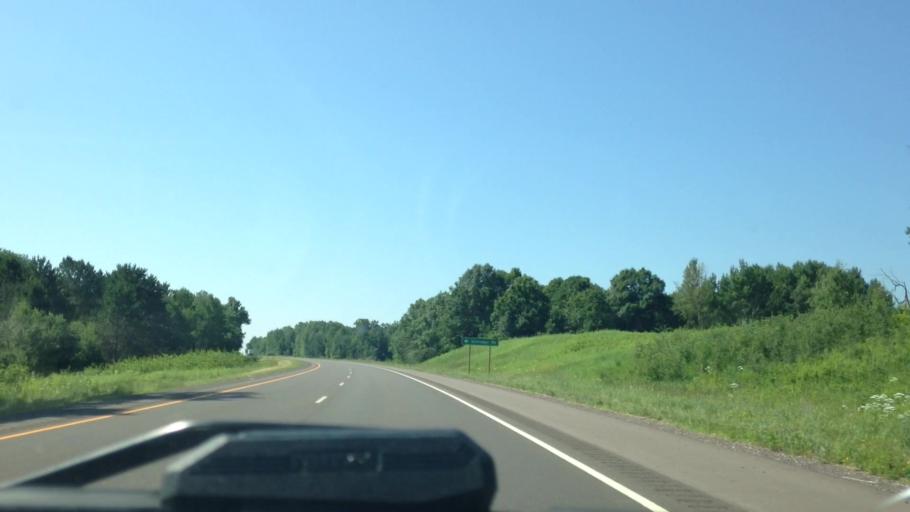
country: US
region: Wisconsin
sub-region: Washburn County
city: Spooner
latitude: 45.9458
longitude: -91.8293
